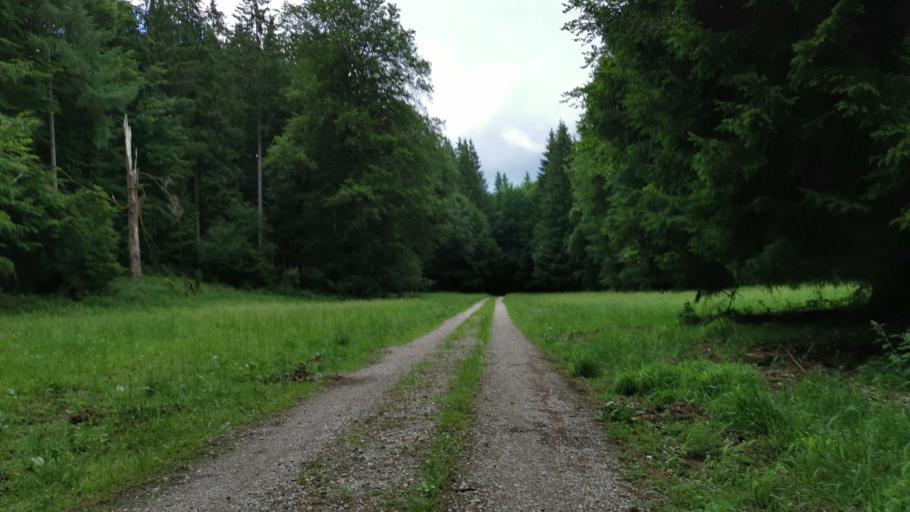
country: DE
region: Bavaria
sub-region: Upper Bavaria
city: Schaftlarn
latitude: 48.0220
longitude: 11.4412
